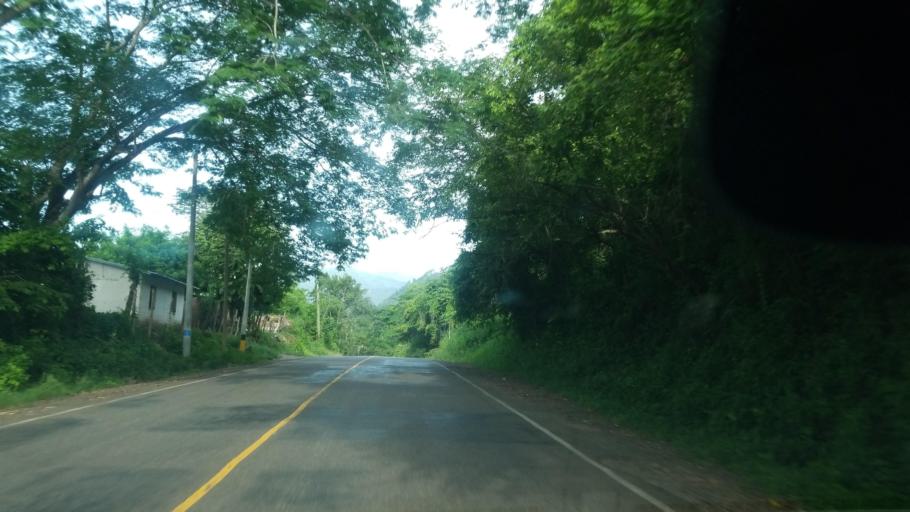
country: HN
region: Santa Barbara
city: Trinidad
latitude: 15.1231
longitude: -88.2065
